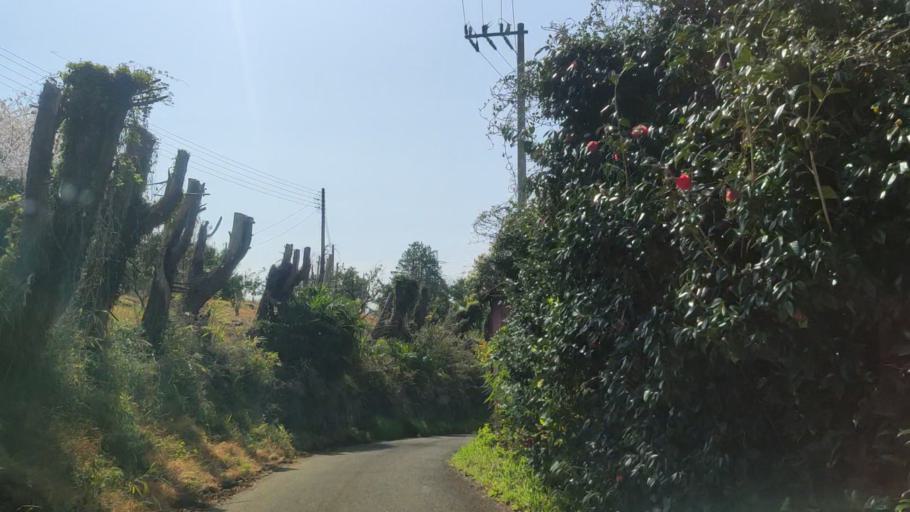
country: JP
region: Kanagawa
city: Ninomiya
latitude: 35.3238
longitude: 139.2712
